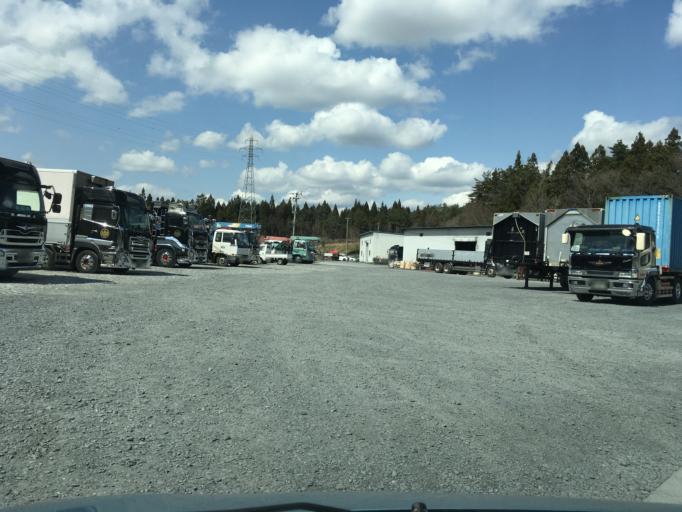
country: JP
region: Iwate
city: Ichinoseki
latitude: 38.8846
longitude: 141.3367
